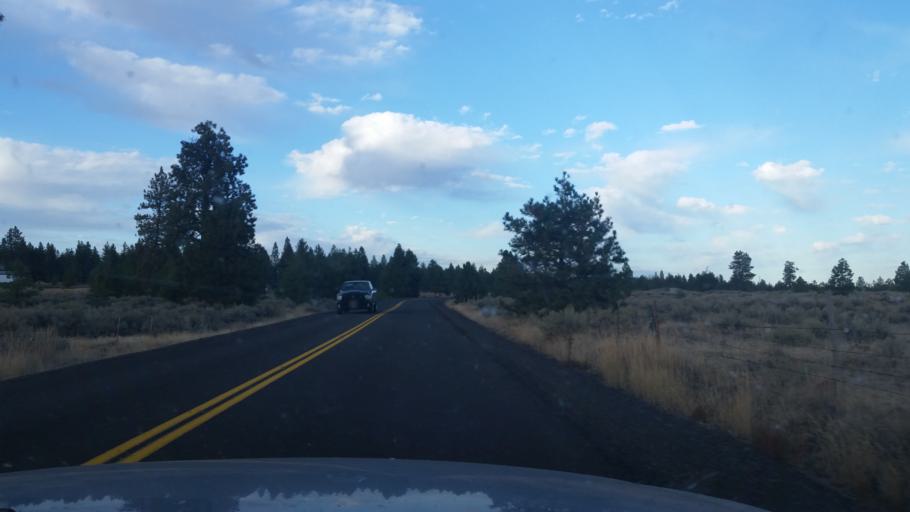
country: US
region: Washington
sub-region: Spokane County
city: Medical Lake
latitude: 47.4513
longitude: -117.8174
